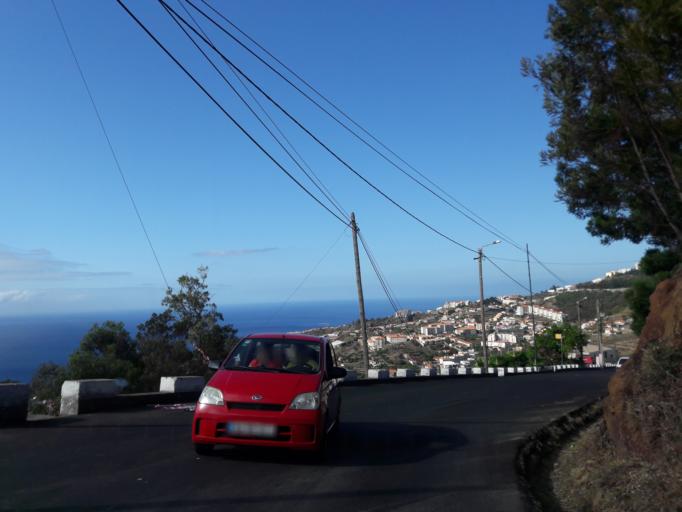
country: PT
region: Madeira
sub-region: Santa Cruz
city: Camacha
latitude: 32.6587
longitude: -16.8358
